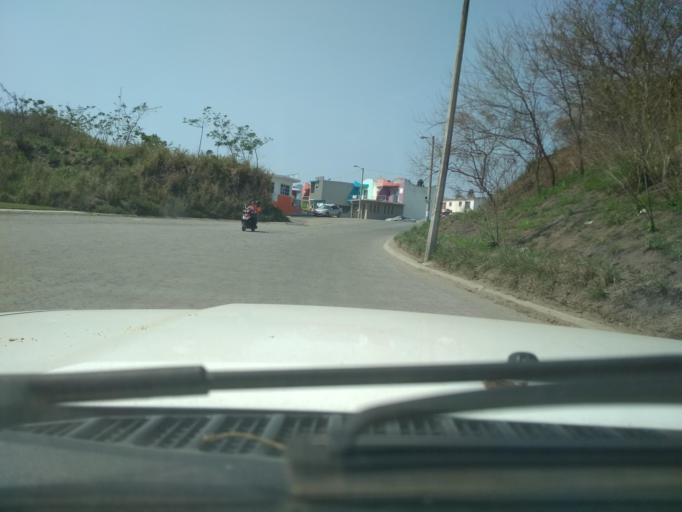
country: MX
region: Veracruz
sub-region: Veracruz
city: Los Torrentes
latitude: 19.1984
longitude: -96.2076
